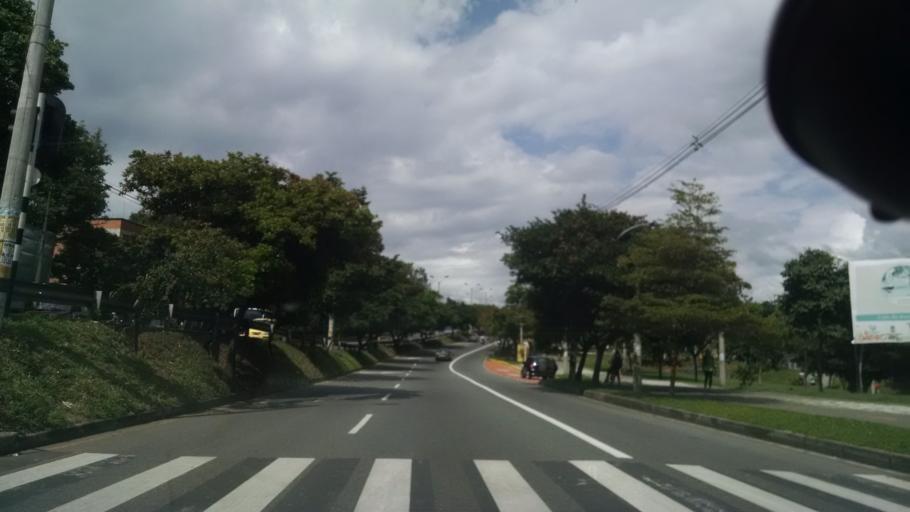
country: CO
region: Antioquia
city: Medellin
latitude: 6.2937
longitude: -75.5688
